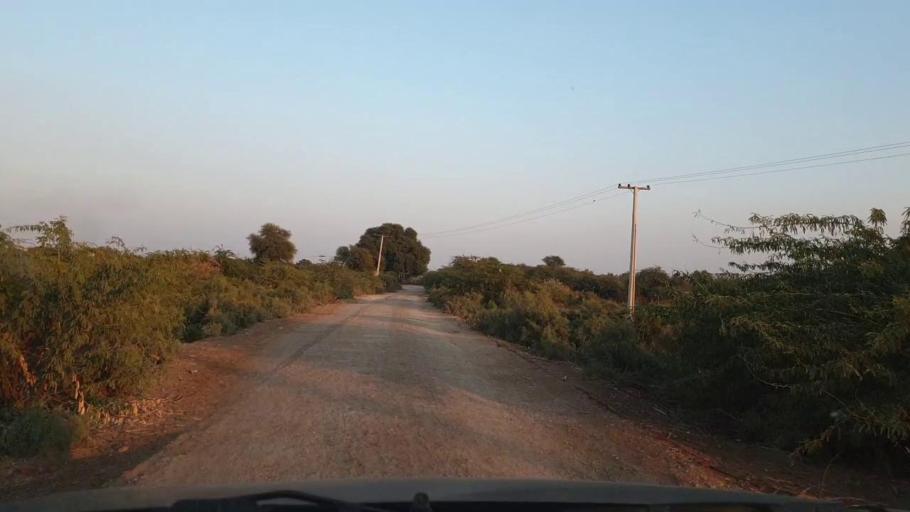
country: PK
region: Sindh
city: Jhol
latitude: 25.9202
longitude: 68.9601
